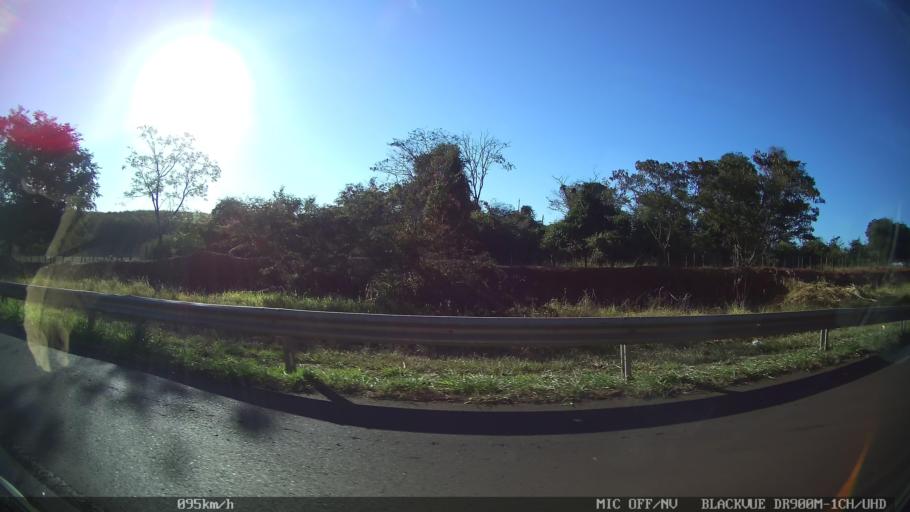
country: BR
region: Sao Paulo
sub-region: Guapiacu
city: Guapiacu
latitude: -20.7684
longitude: -49.2069
